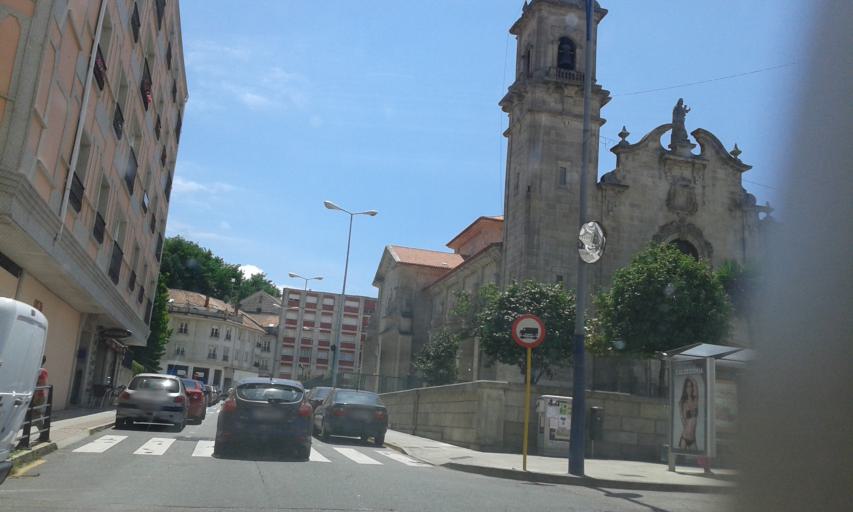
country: ES
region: Galicia
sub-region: Provincia de Pontevedra
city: Marin
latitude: 42.3916
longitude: -8.6994
